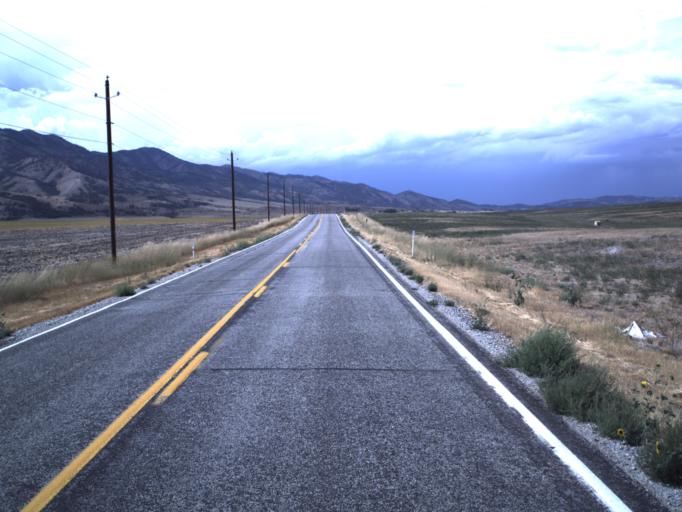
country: US
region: Utah
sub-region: Cache County
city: Benson
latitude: 41.8837
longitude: -112.0307
